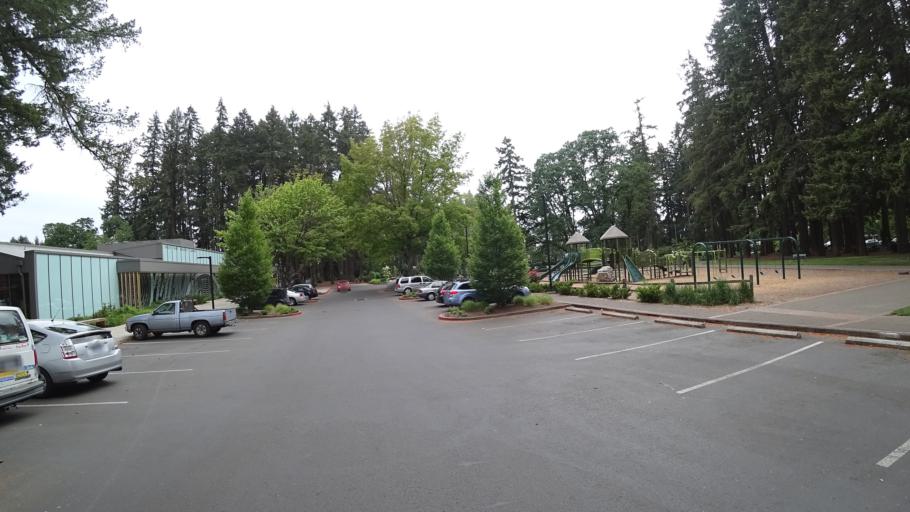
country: US
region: Oregon
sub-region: Washington County
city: Hillsboro
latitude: 45.5146
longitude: -122.9757
